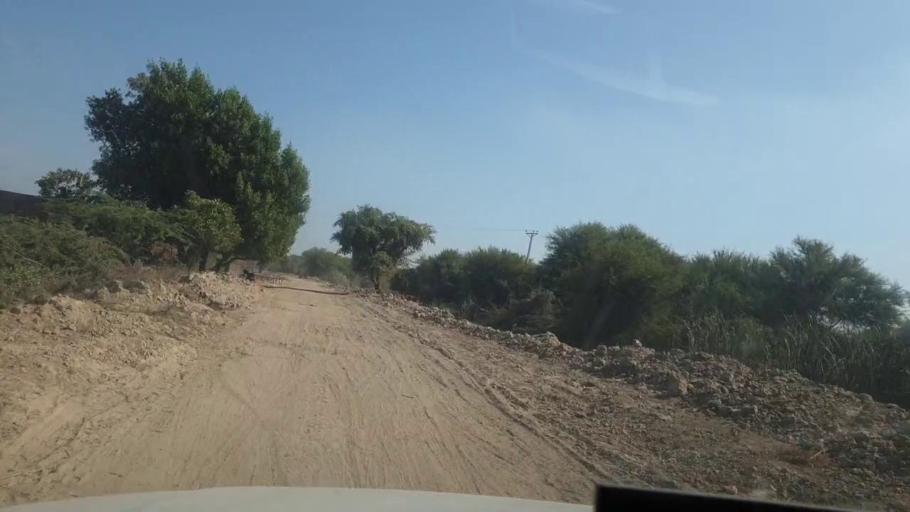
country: PK
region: Sindh
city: Kotri
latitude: 25.1605
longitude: 68.3055
